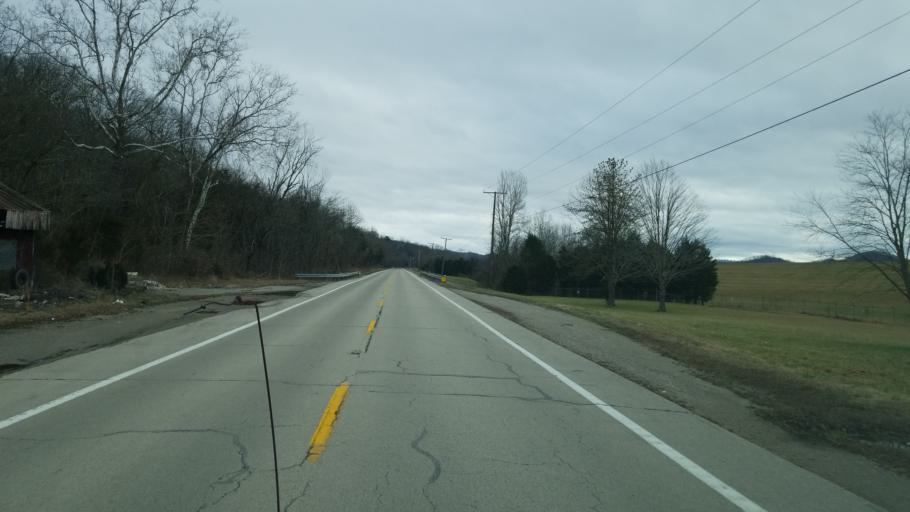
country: US
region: Ohio
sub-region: Adams County
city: West Union
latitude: 38.6930
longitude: -83.4720
